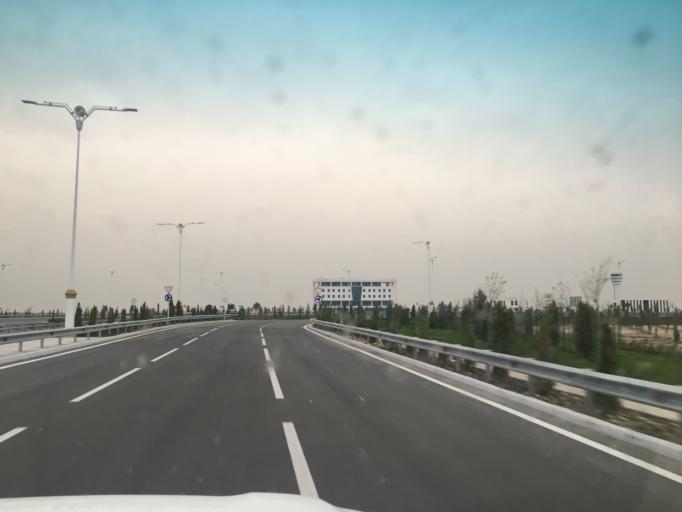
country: TM
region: Lebap
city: Turkmenabat
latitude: 38.9412
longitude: 63.5700
